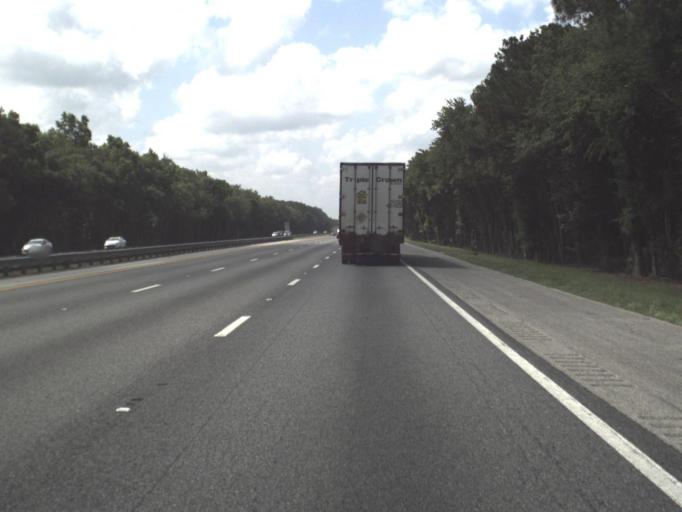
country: US
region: Florida
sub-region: Saint Johns County
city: Fruit Cove
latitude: 30.0232
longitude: -81.4840
